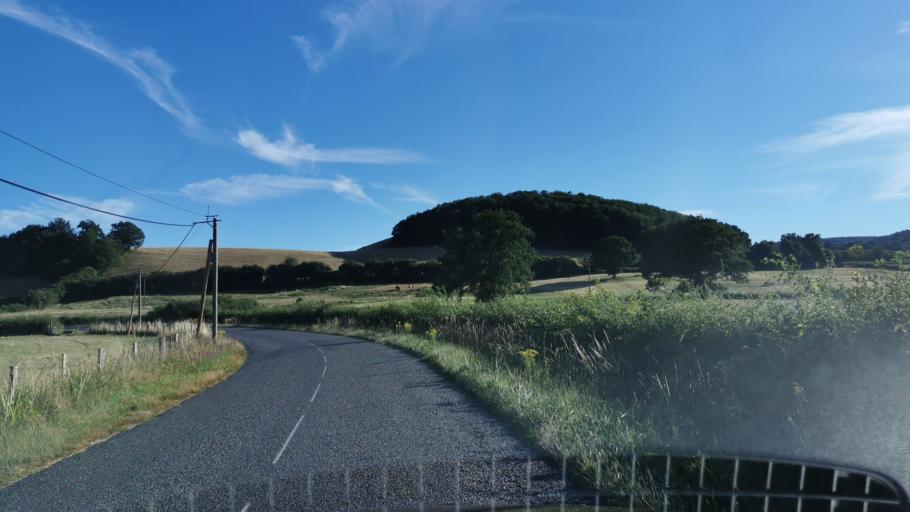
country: FR
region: Bourgogne
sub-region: Departement de Saone-et-Loire
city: Marmagne
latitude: 46.8135
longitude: 4.3269
